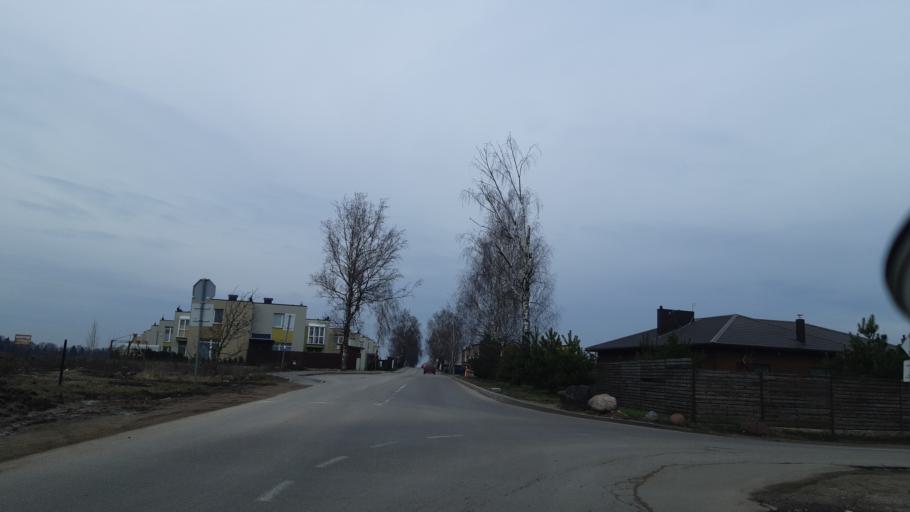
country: LT
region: Kauno apskritis
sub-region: Kauno rajonas
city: Akademija (Kaunas)
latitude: 54.9474
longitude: 23.8286
